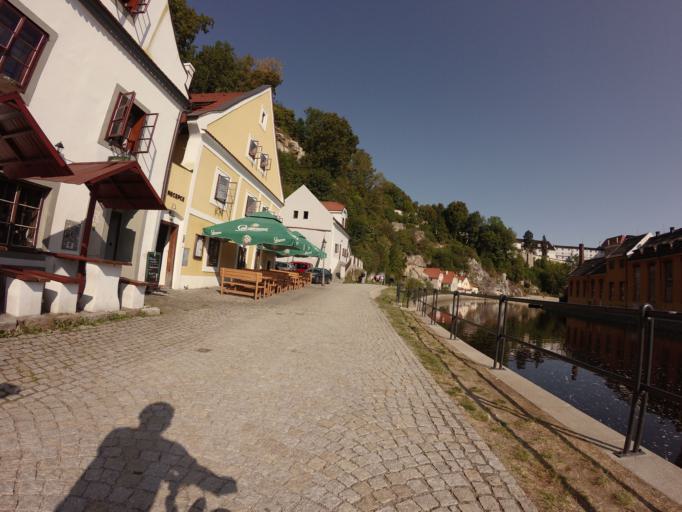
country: CZ
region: Jihocesky
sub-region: Okres Cesky Krumlov
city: Cesky Krumlov
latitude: 48.8094
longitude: 14.3127
